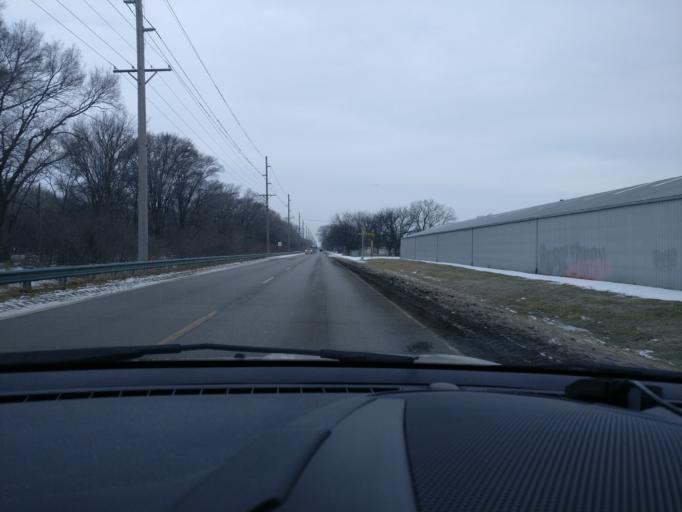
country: US
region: Nebraska
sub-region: Dodge County
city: Fremont
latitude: 41.4389
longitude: -96.5247
